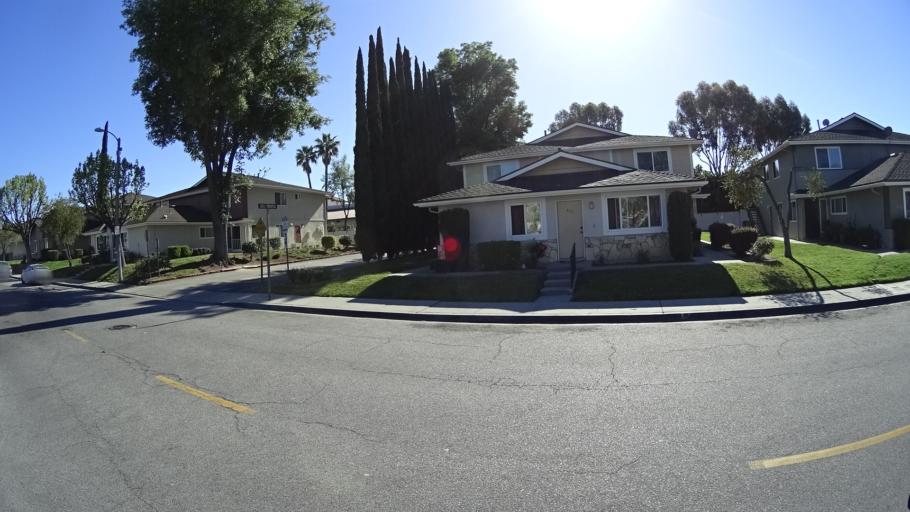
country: US
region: California
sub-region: Ventura County
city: Casa Conejo
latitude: 34.1864
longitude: -118.9134
